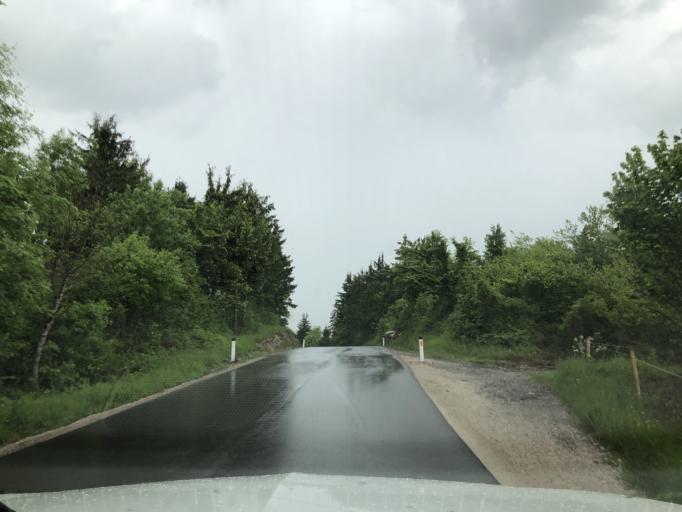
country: SI
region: Postojna
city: Postojna
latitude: 45.7952
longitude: 14.2435
